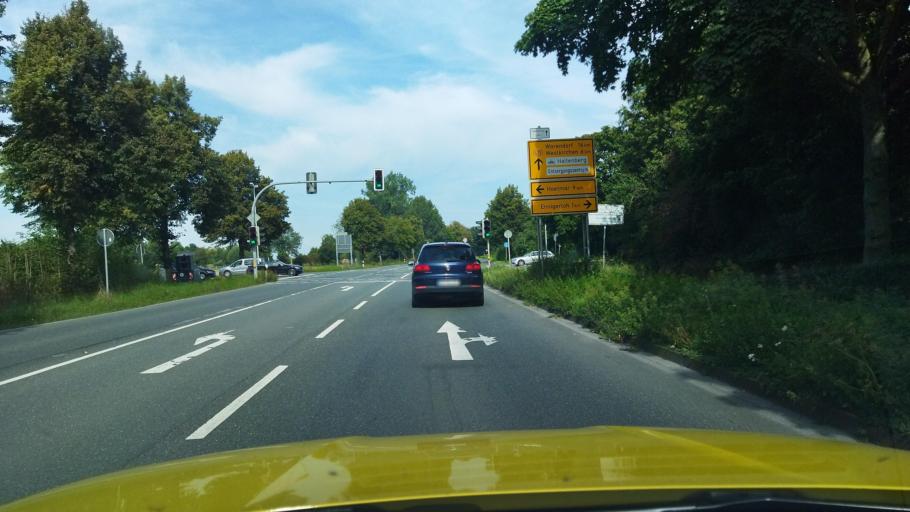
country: DE
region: North Rhine-Westphalia
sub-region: Regierungsbezirk Munster
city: Ennigerloh
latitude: 51.8388
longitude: 8.0160
